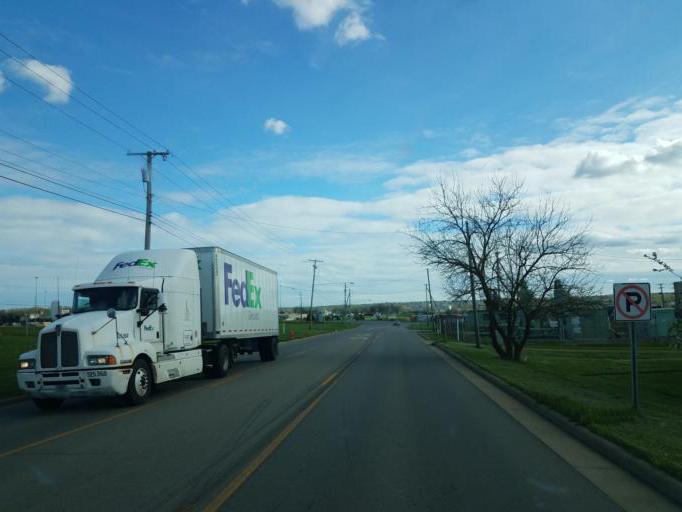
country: US
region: Ohio
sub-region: Richland County
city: Mansfield
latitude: 40.7970
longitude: -82.5135
